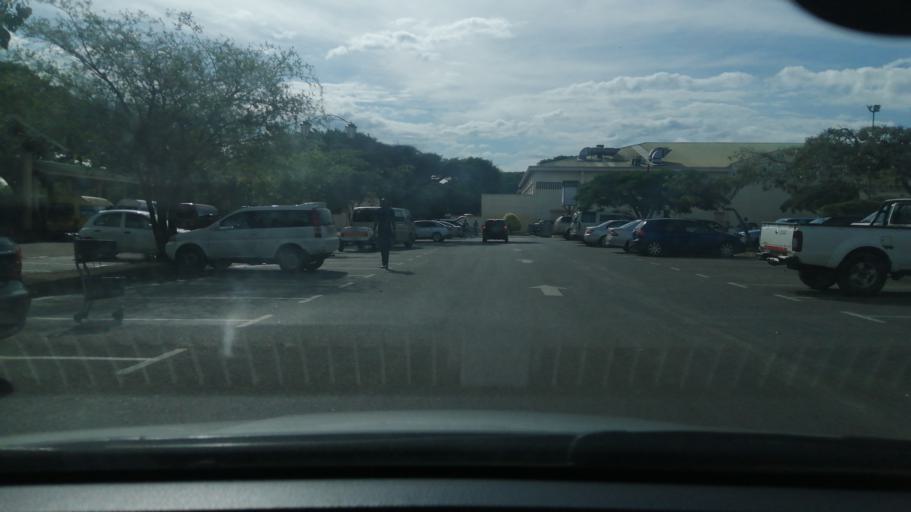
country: ZW
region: Harare
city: Harare
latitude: -17.7655
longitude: 30.9786
